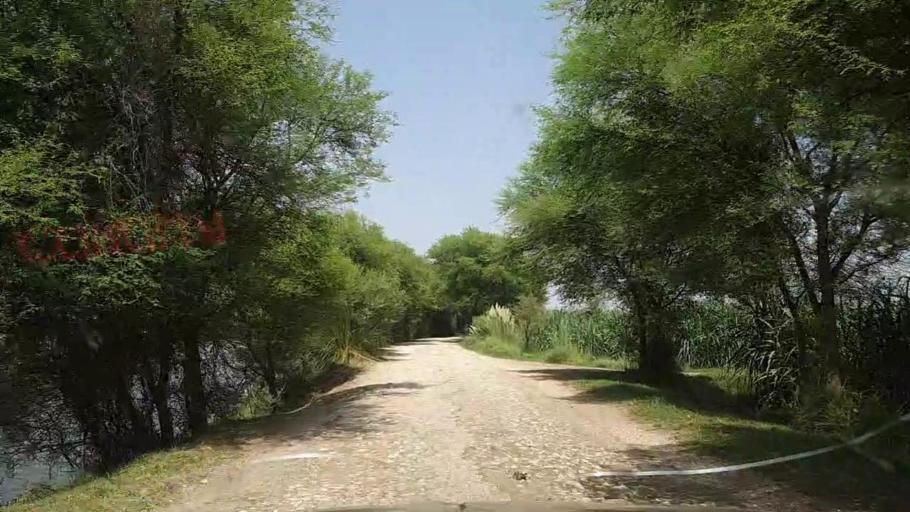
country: PK
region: Sindh
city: Ghotki
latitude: 28.0907
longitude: 69.3116
